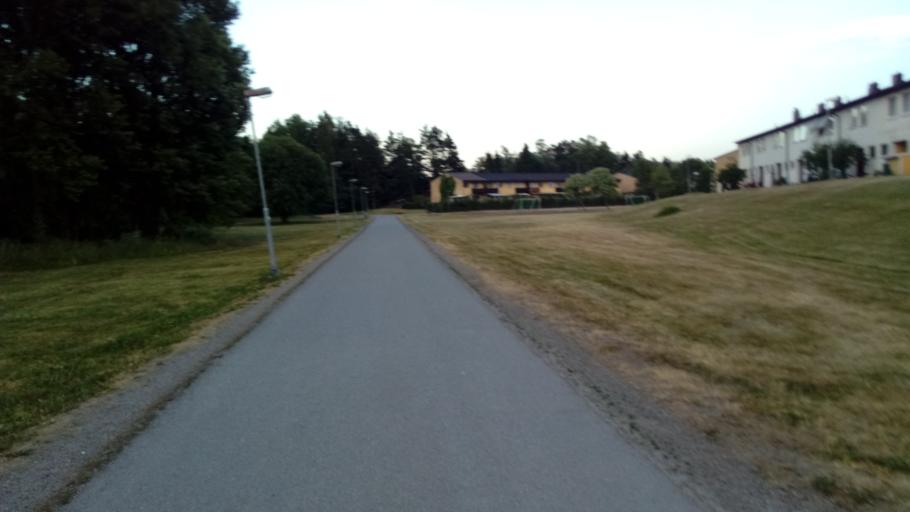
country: SE
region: Stockholm
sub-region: Tyreso Kommun
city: Bollmora
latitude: 59.2446
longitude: 18.2402
